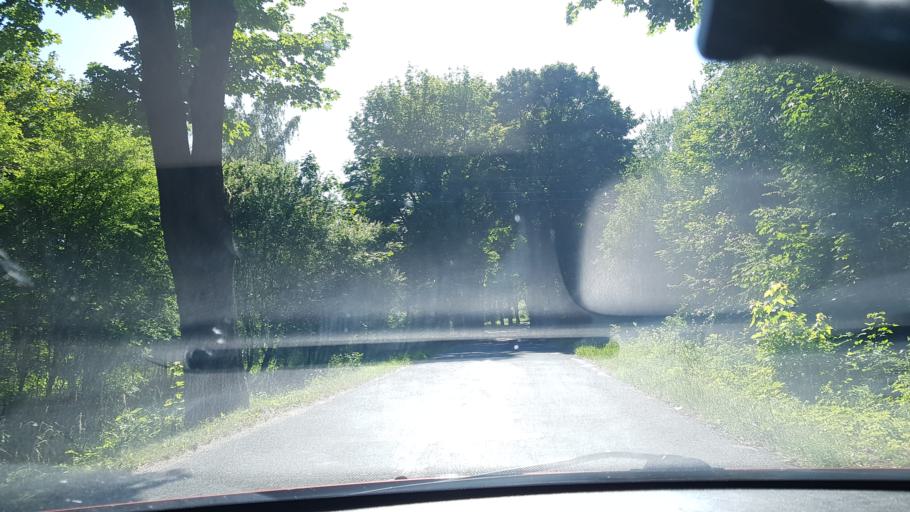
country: PL
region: Lower Silesian Voivodeship
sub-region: Powiat klodzki
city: Miedzylesie
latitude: 50.2292
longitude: 16.7443
